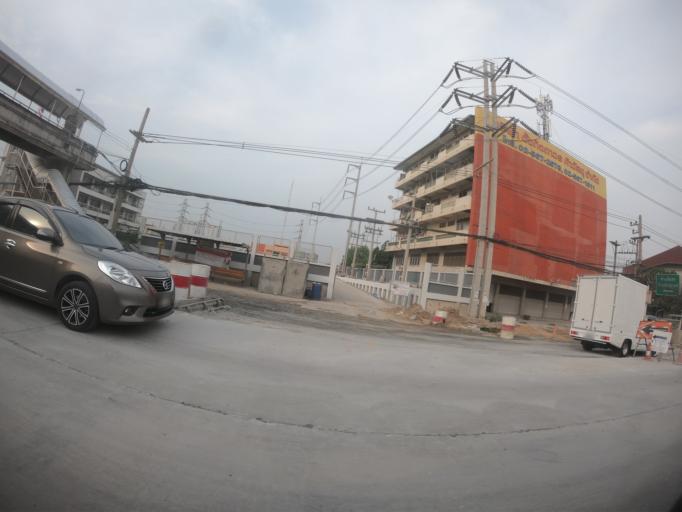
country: TH
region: Phra Nakhon Si Ayutthaya
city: Ban Bang Kadi Pathum Thani
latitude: 13.9904
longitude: 100.5812
